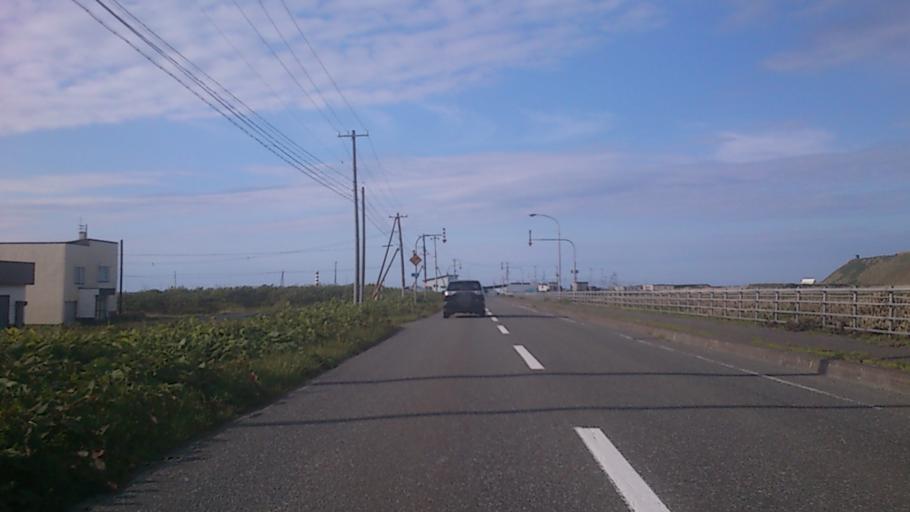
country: JP
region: Hokkaido
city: Wakkanai
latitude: 45.4364
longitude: 141.6408
